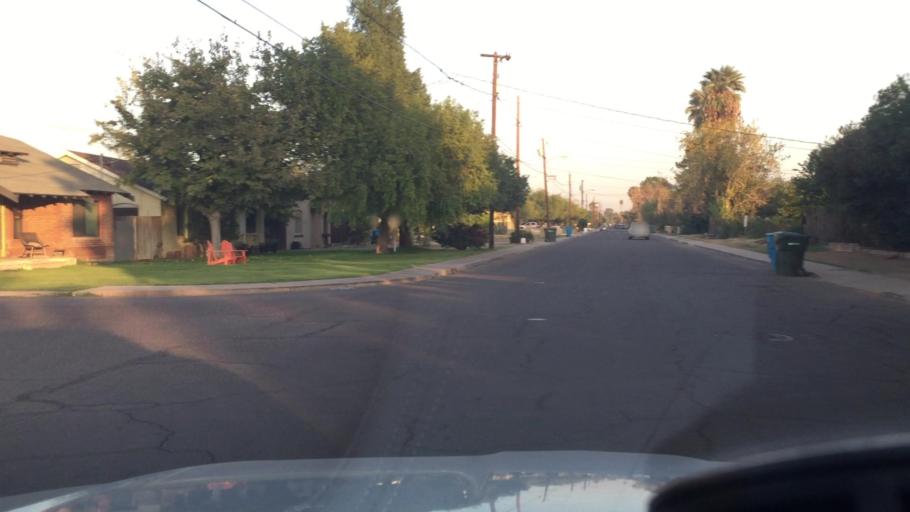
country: US
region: Arizona
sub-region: Maricopa County
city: Phoenix
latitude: 33.4893
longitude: -112.0634
